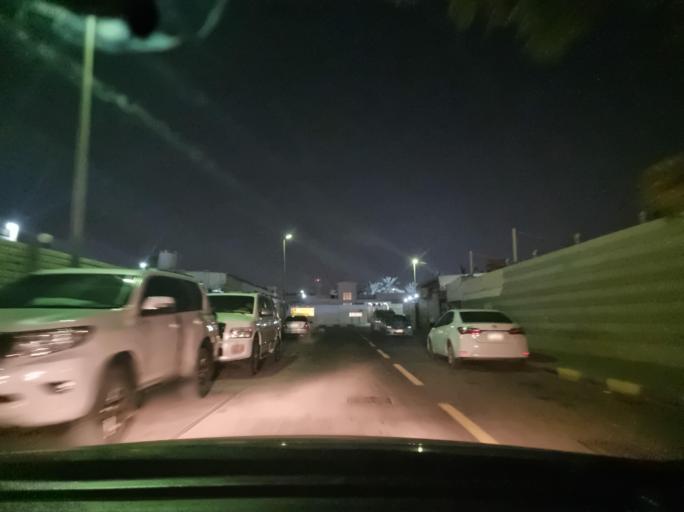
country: AE
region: Ash Shariqah
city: Sharjah
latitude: 25.3694
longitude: 55.4236
